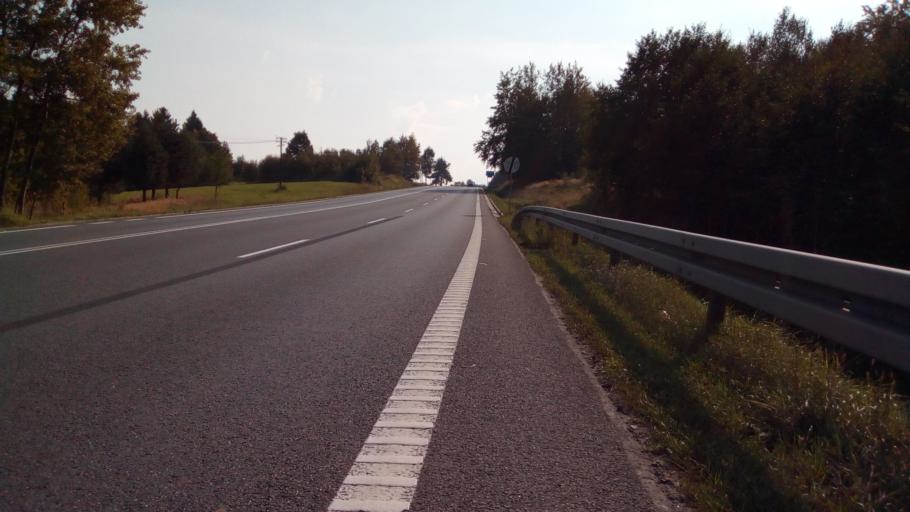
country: PL
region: Subcarpathian Voivodeship
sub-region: Powiat strzyzowski
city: Jawornik
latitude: 49.8420
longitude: 21.8895
